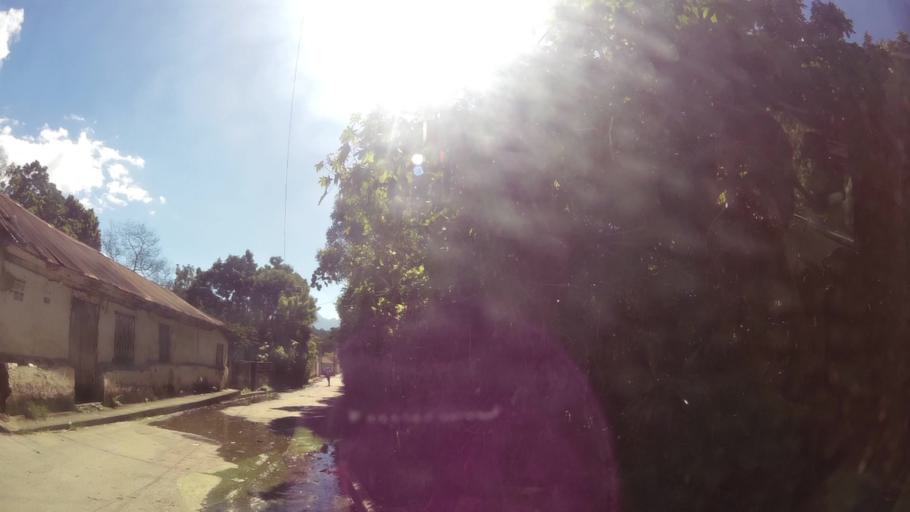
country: GT
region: Guatemala
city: Petapa
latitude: 14.4936
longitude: -90.5548
